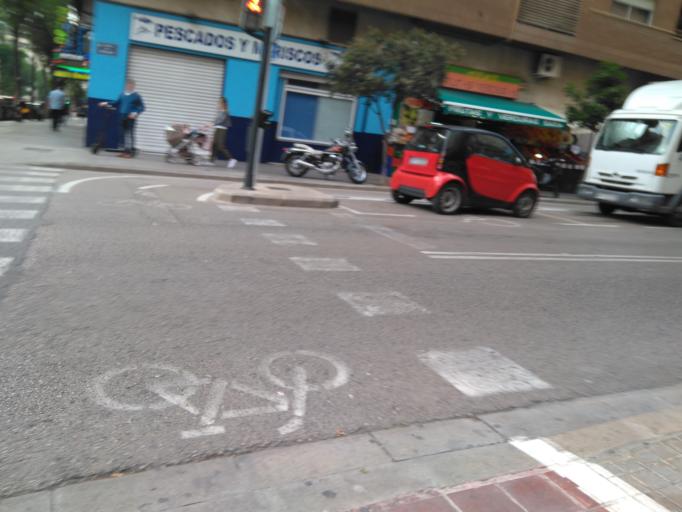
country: ES
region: Valencia
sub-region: Provincia de Valencia
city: Valencia
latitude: 39.4840
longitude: -0.3835
